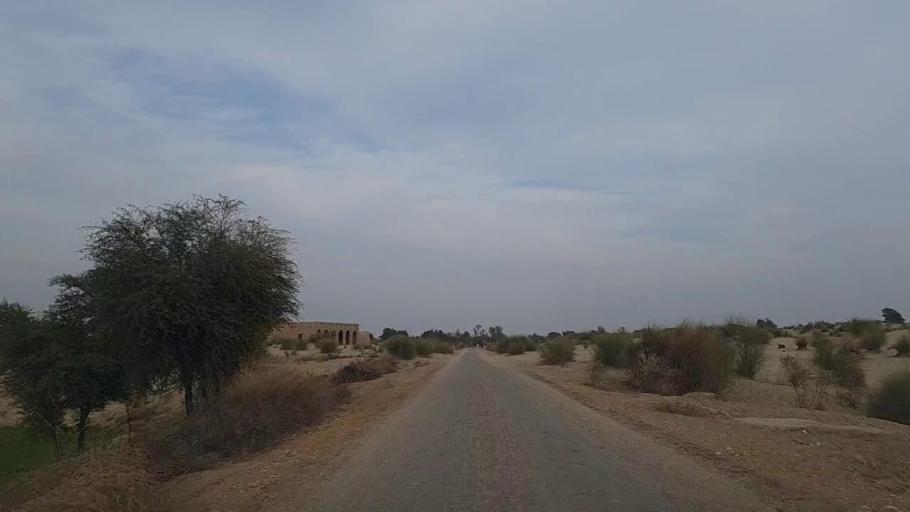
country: PK
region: Sindh
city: Daur
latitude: 26.5116
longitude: 68.4673
